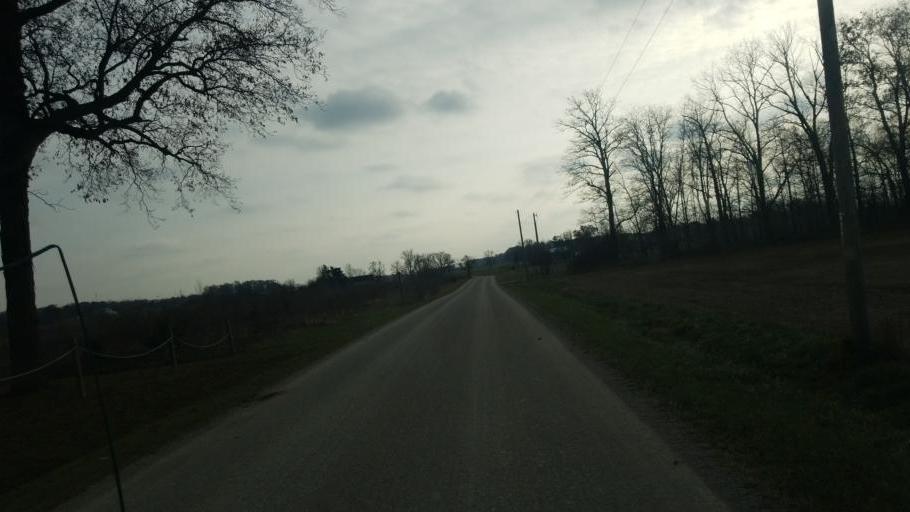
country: US
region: Indiana
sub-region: Adams County
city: Geneva
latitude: 40.6146
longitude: -84.9672
